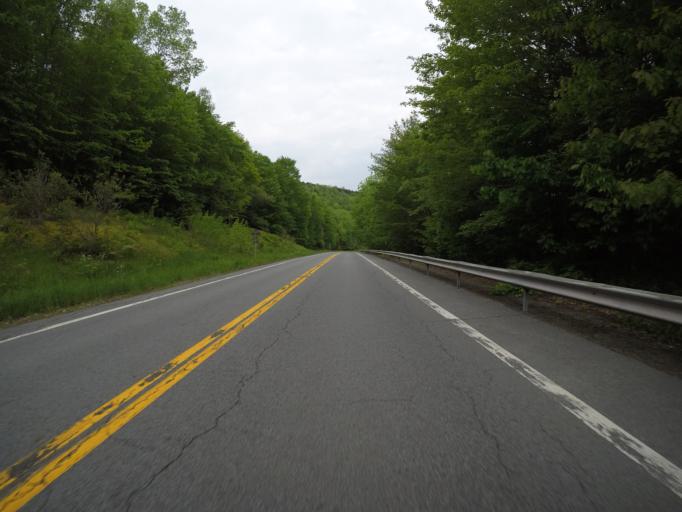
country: US
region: New York
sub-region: Sullivan County
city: Livingston Manor
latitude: 42.0717
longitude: -74.8355
